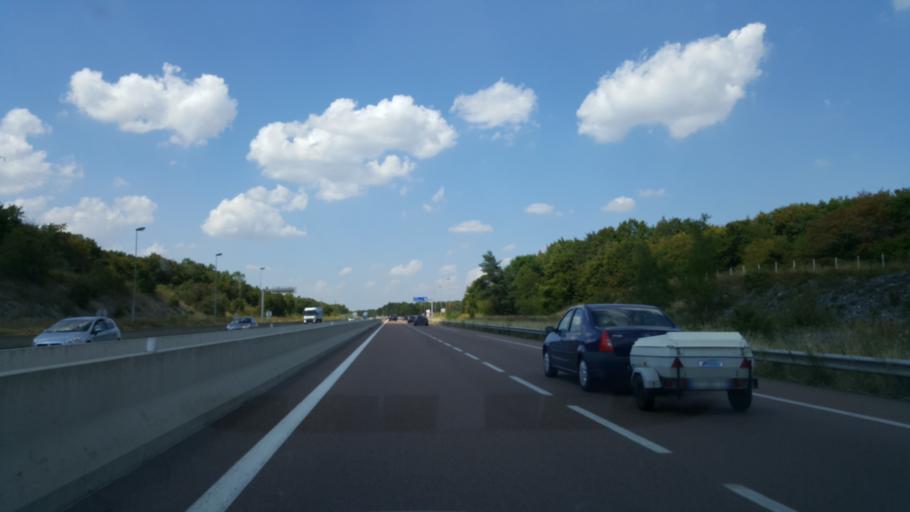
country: FR
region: Bourgogne
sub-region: Departement de la Cote-d'Or
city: Savigny-les-Beaune
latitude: 47.1075
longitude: 4.7136
